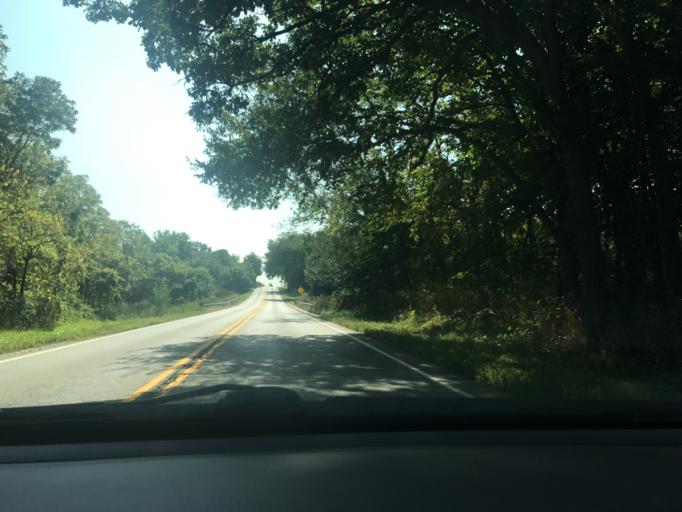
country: US
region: Illinois
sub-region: Kane County
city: Pingree Grove
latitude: 42.0654
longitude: -88.4313
